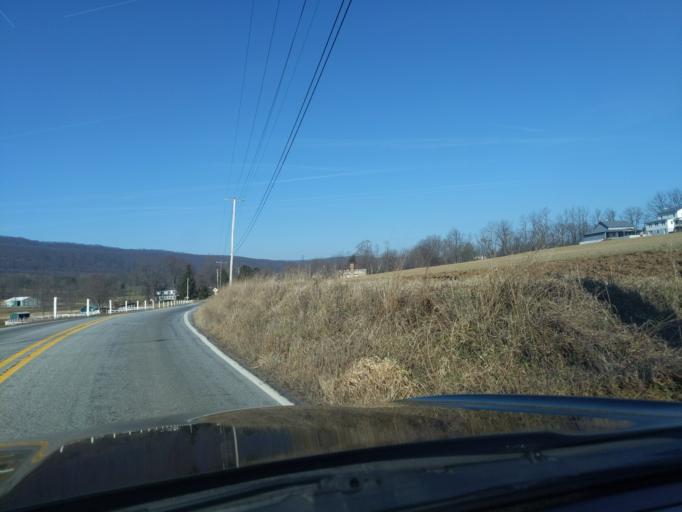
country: US
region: Pennsylvania
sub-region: Blair County
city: Tipton
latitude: 40.5884
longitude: -78.2657
